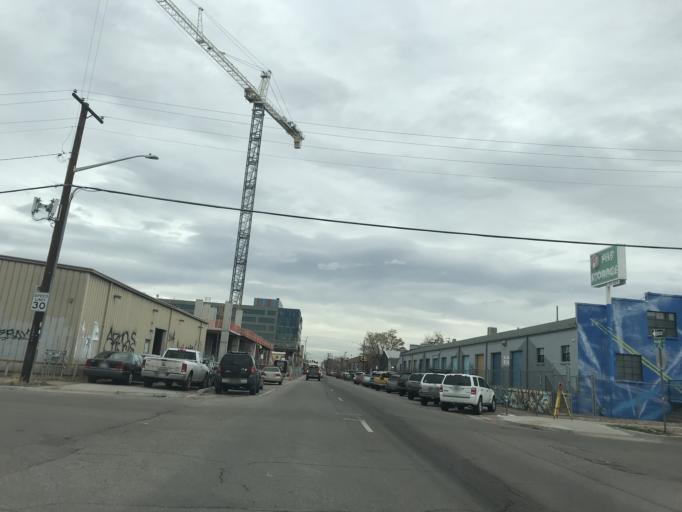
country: US
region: Colorado
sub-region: Denver County
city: Denver
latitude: 39.7666
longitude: -104.9767
